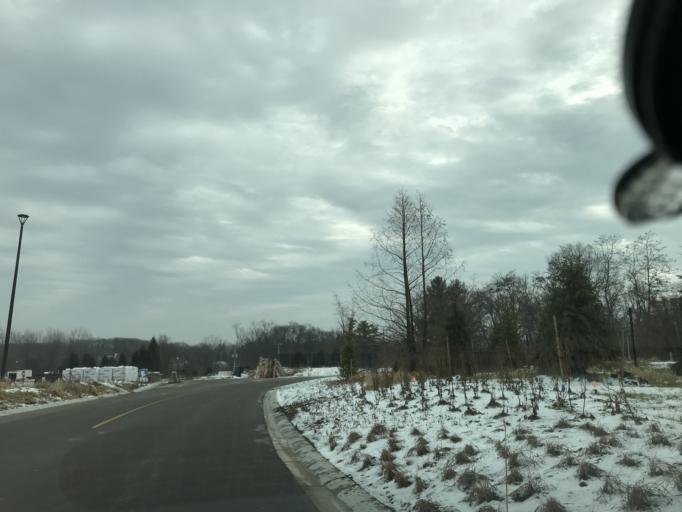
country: US
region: Michigan
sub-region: Kent County
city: East Grand Rapids
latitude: 42.9776
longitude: -85.5853
